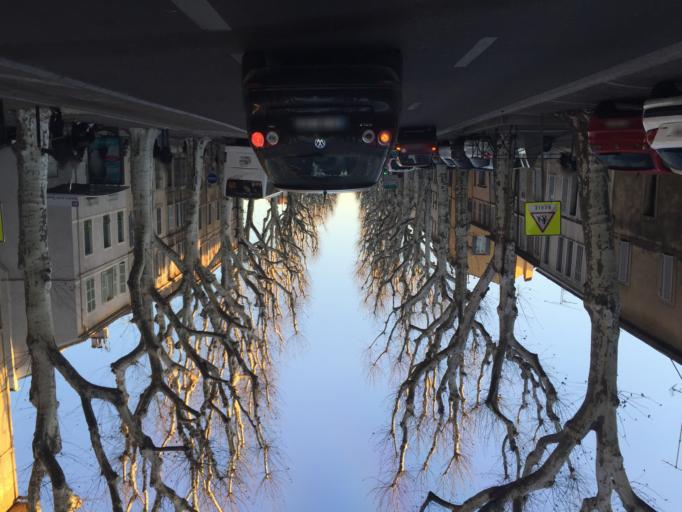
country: FR
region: Provence-Alpes-Cote d'Azur
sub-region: Departement des Bouches-du-Rhone
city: Aix-en-Provence
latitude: 43.5298
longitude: 5.4532
